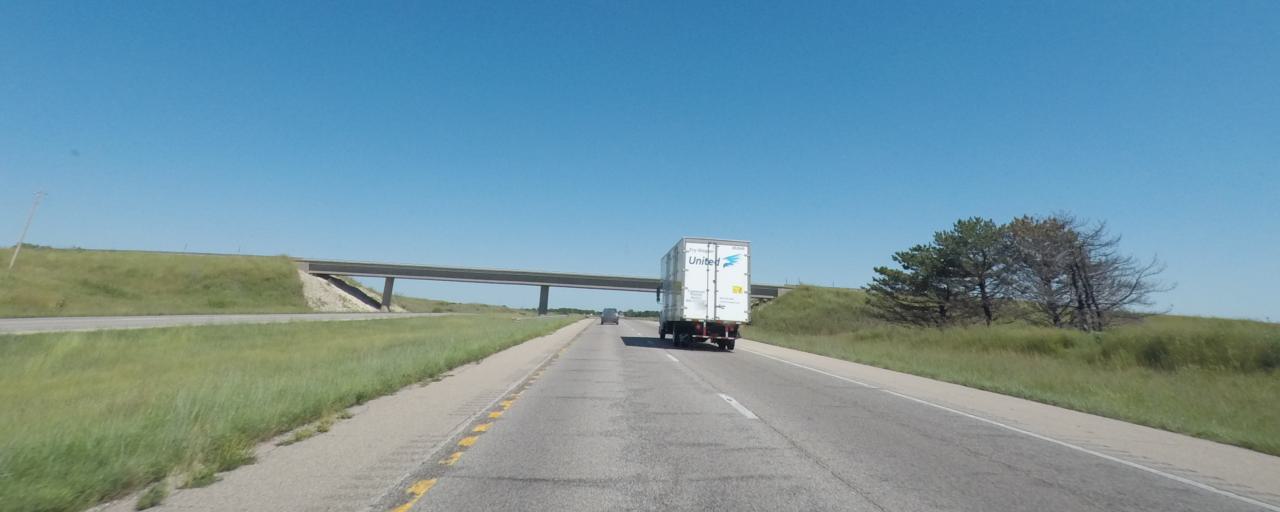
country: US
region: Kansas
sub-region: Osage County
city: Lyndon
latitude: 38.4265
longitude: -95.7859
